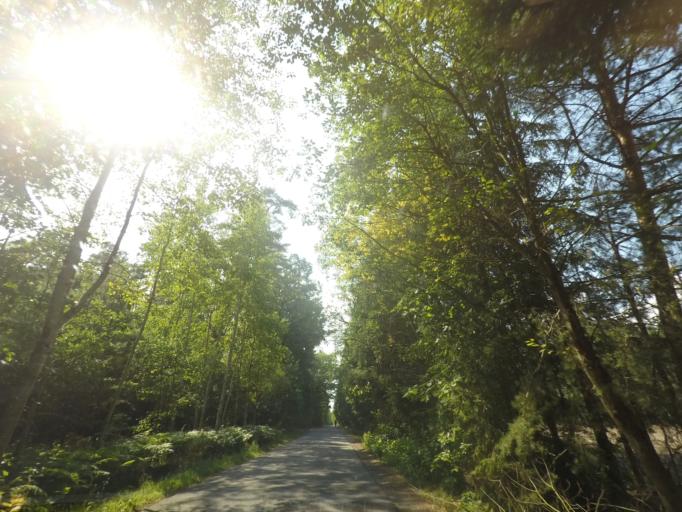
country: CZ
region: Pardubicky
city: Horni Jeleni
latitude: 50.0636
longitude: 16.0824
